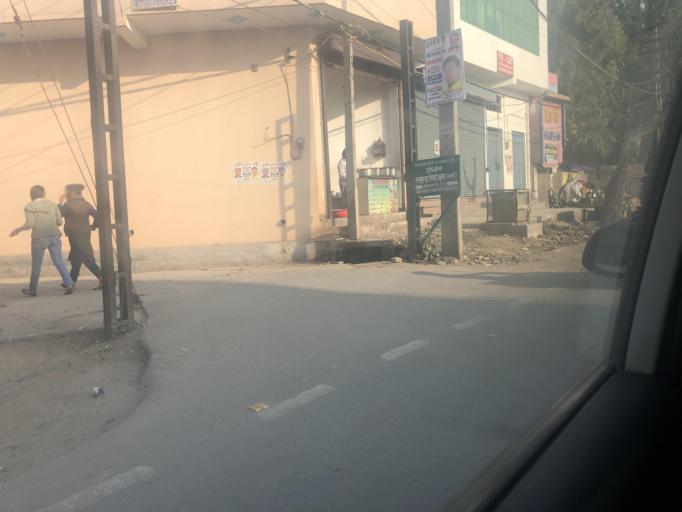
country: IN
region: Haryana
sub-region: Jhajjar
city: Bahadurgarh
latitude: 28.6160
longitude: 76.9759
